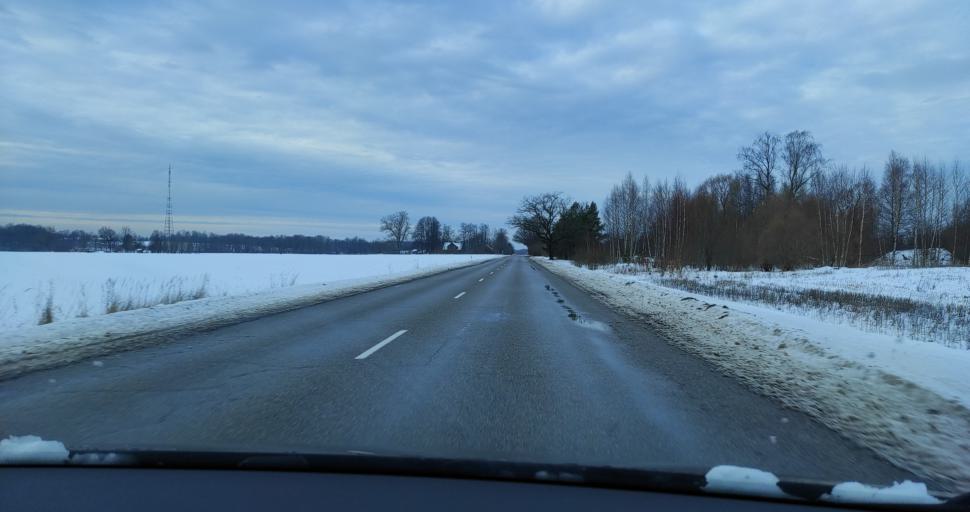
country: LV
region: Kuldigas Rajons
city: Kuldiga
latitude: 56.9303
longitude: 22.0428
